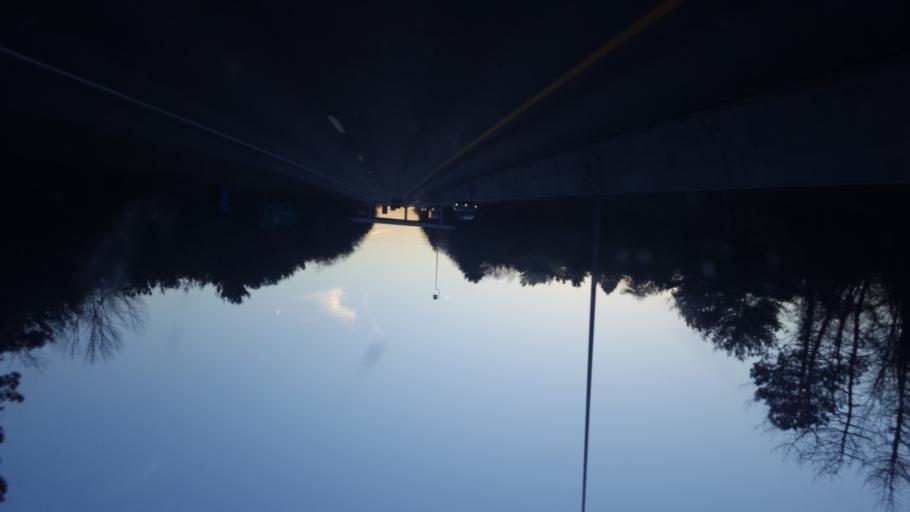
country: US
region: Ohio
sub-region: Belmont County
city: Saint Clairsville
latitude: 40.0711
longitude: -80.9090
